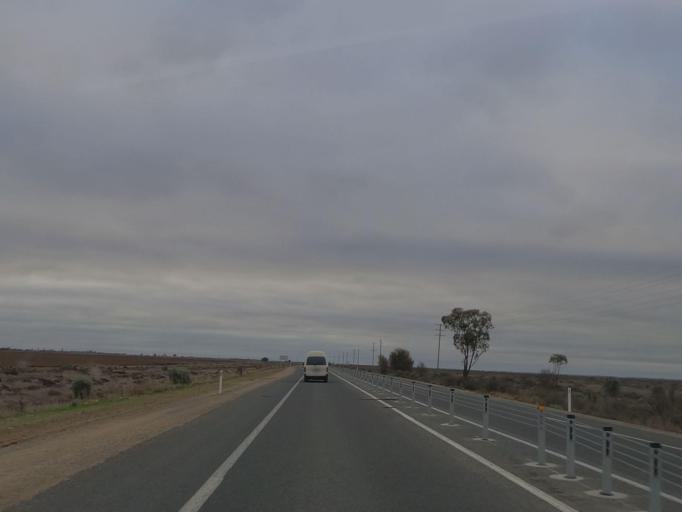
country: AU
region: Victoria
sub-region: Swan Hill
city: Swan Hill
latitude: -35.5173
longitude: 143.7290
